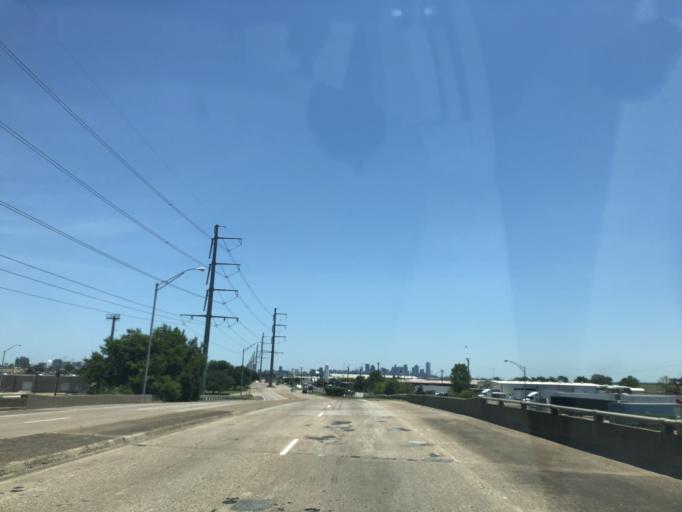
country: US
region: Texas
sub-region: Dallas County
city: Irving
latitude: 32.8084
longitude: -96.9011
